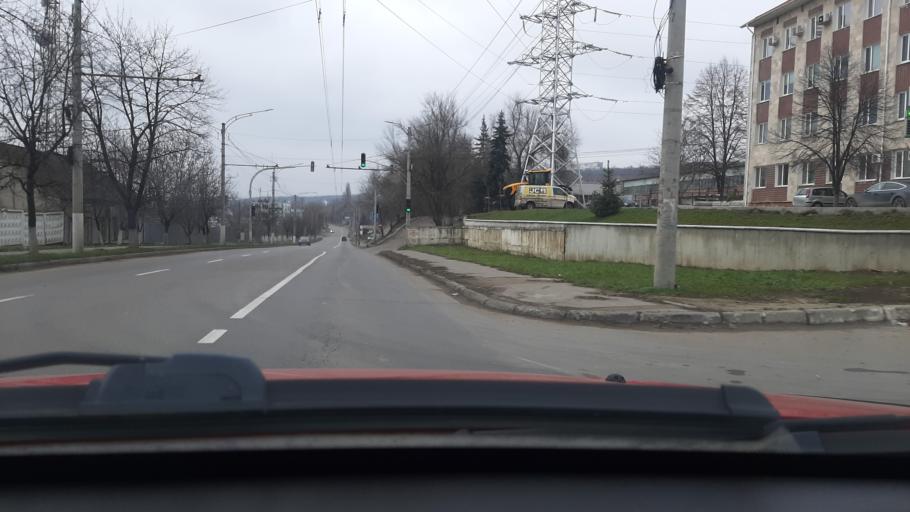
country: MD
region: Chisinau
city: Chisinau
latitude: 47.0457
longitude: 28.8302
